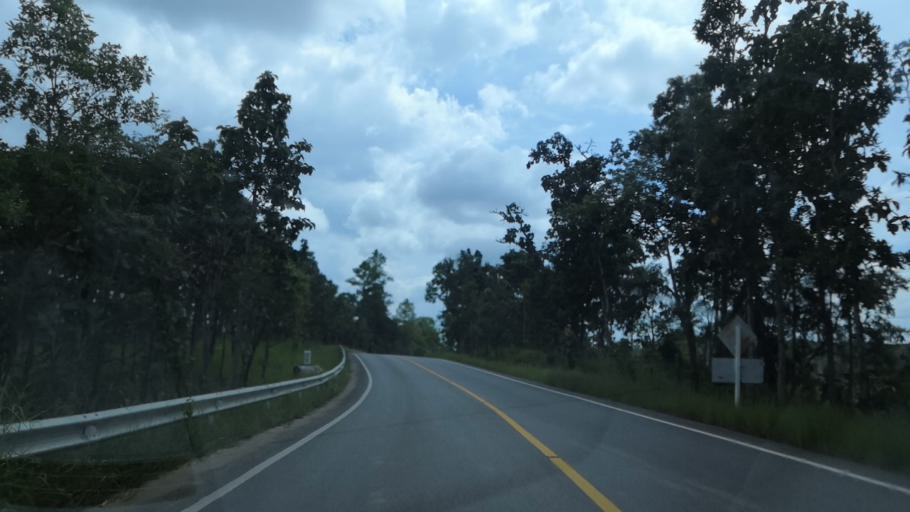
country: TH
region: Mae Hong Son
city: Khun Yuam
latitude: 18.8011
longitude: 97.9311
